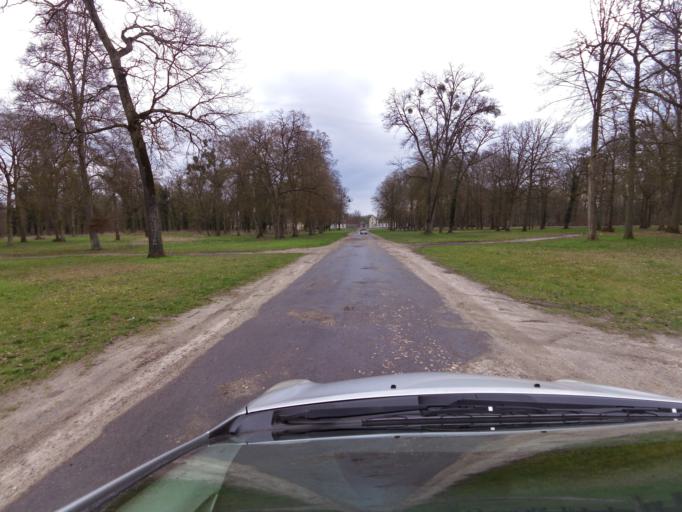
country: FR
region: Picardie
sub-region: Departement de l'Oise
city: Ver-sur-Launette
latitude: 49.1465
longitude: 2.6797
